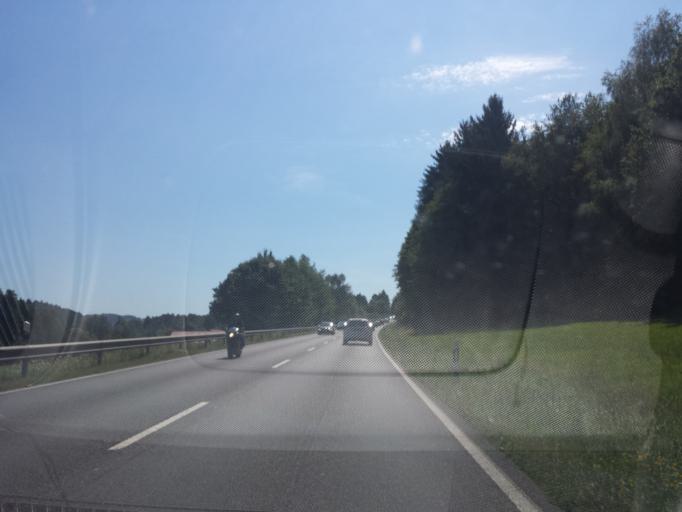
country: DE
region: Bavaria
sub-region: Upper Palatinate
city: Traitsching
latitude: 49.1324
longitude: 12.6528
